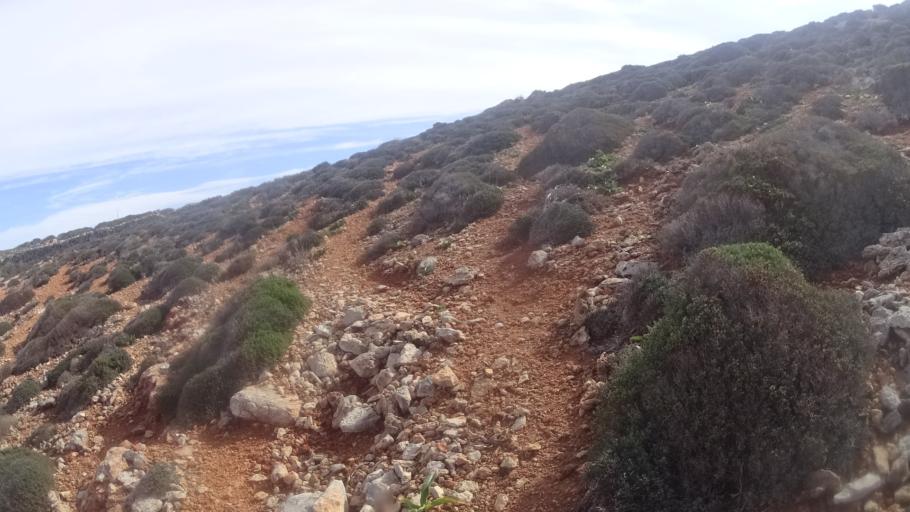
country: MT
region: Il-Qala
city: Qala
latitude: 36.0096
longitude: 14.3298
